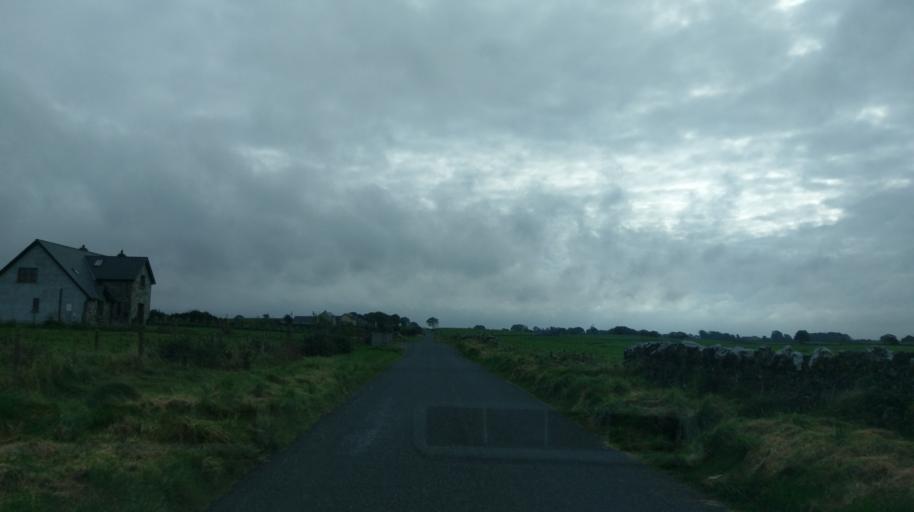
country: IE
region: Connaught
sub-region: County Galway
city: Athenry
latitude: 53.4604
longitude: -8.6217
